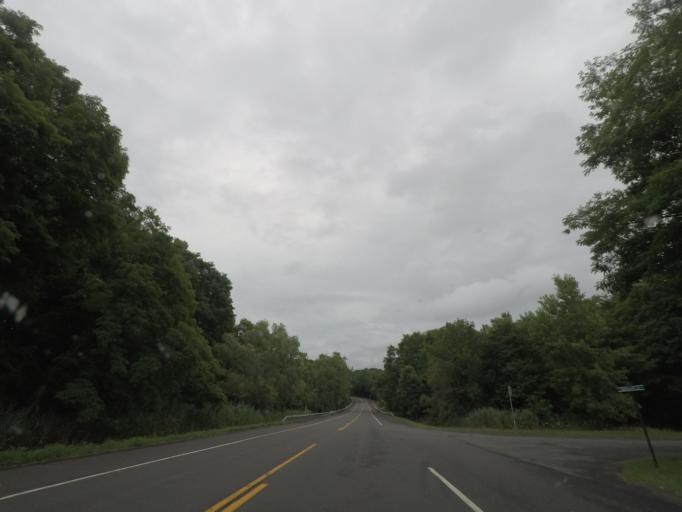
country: US
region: New York
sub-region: Rensselaer County
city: Hampton Manor
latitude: 42.6329
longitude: -73.7287
